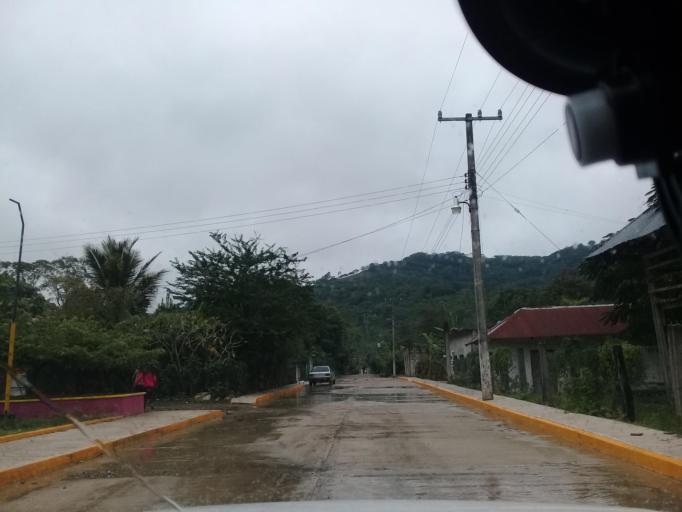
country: MX
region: Veracruz
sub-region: Chalma
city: San Pedro Coyutla
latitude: 21.2238
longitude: -98.4298
